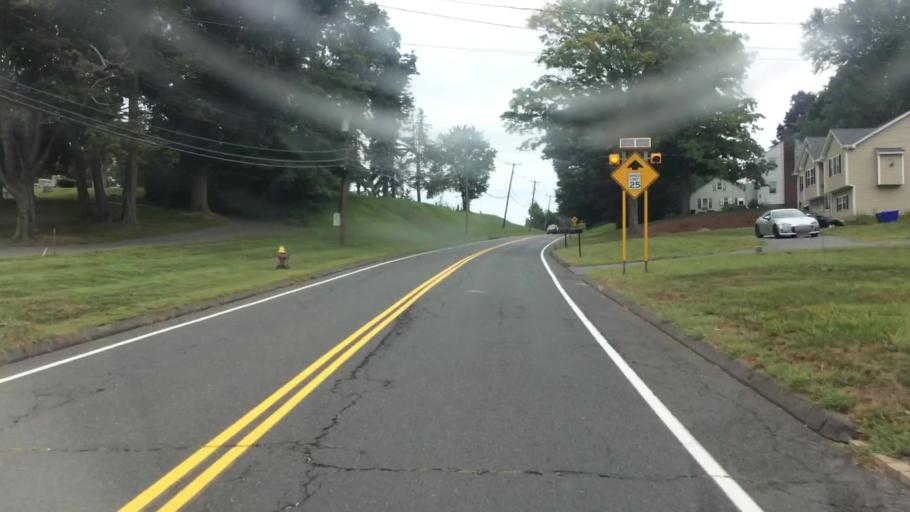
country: US
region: Connecticut
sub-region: Hartford County
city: Glastonbury Center
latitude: 41.6592
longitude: -72.6368
